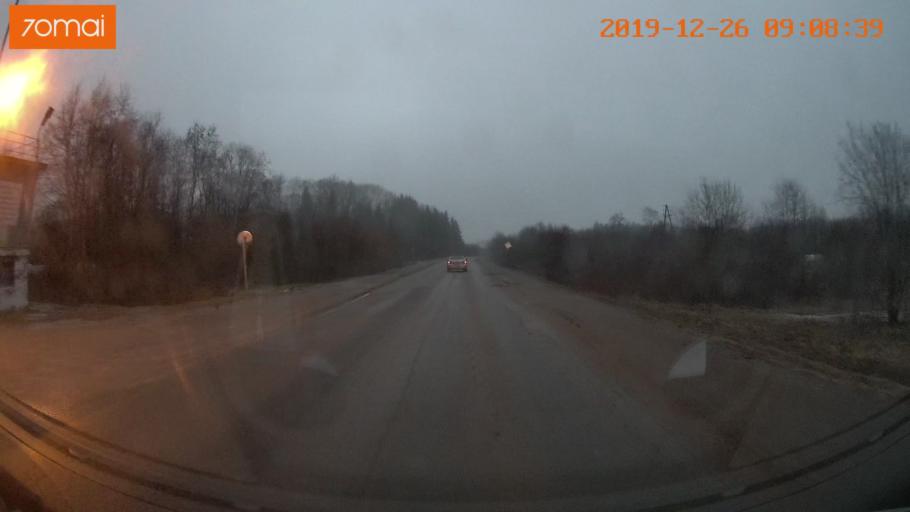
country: RU
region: Vologda
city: Gryazovets
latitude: 58.8589
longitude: 40.2488
